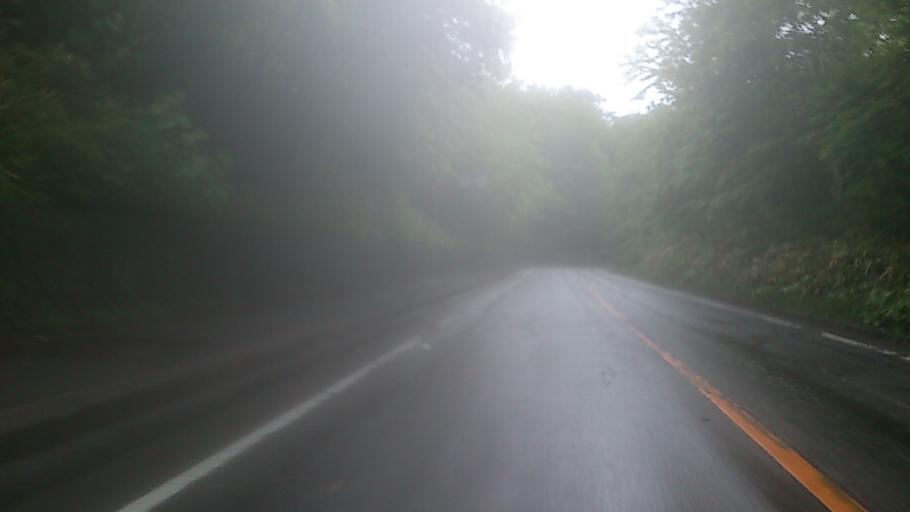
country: JP
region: Hokkaido
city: Shiraoi
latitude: 42.7702
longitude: 141.4124
